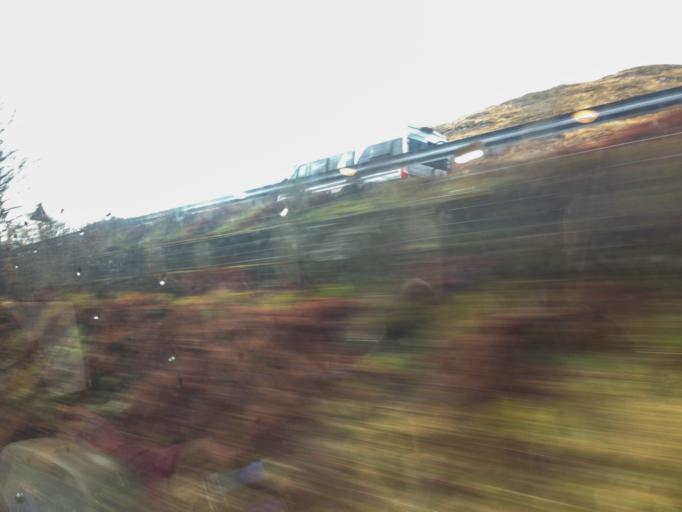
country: GB
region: Scotland
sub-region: Argyll and Bute
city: Isle Of Mull
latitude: 56.9899
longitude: -5.8260
